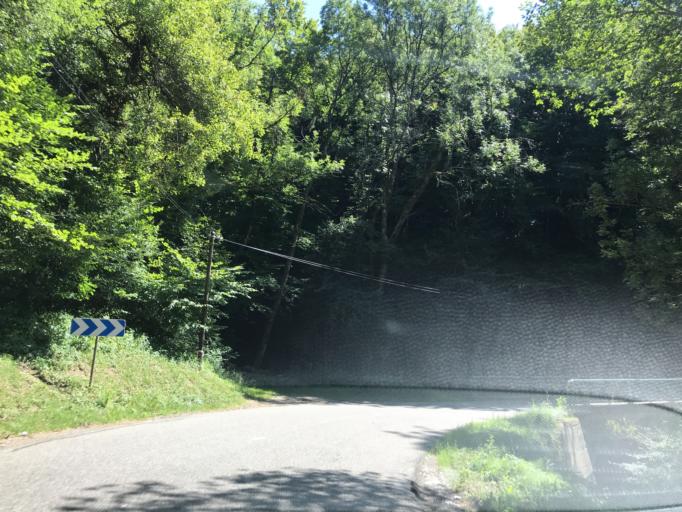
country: FR
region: Rhone-Alpes
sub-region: Departement de la Haute-Savoie
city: Villaz
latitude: 45.9606
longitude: 6.2164
